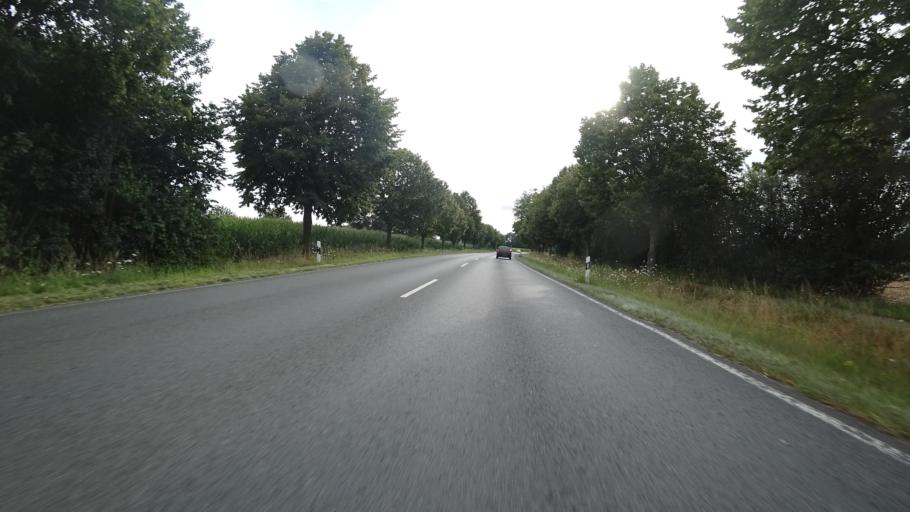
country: DE
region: North Rhine-Westphalia
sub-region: Regierungsbezirk Munster
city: Beelen
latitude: 51.9805
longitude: 8.1270
